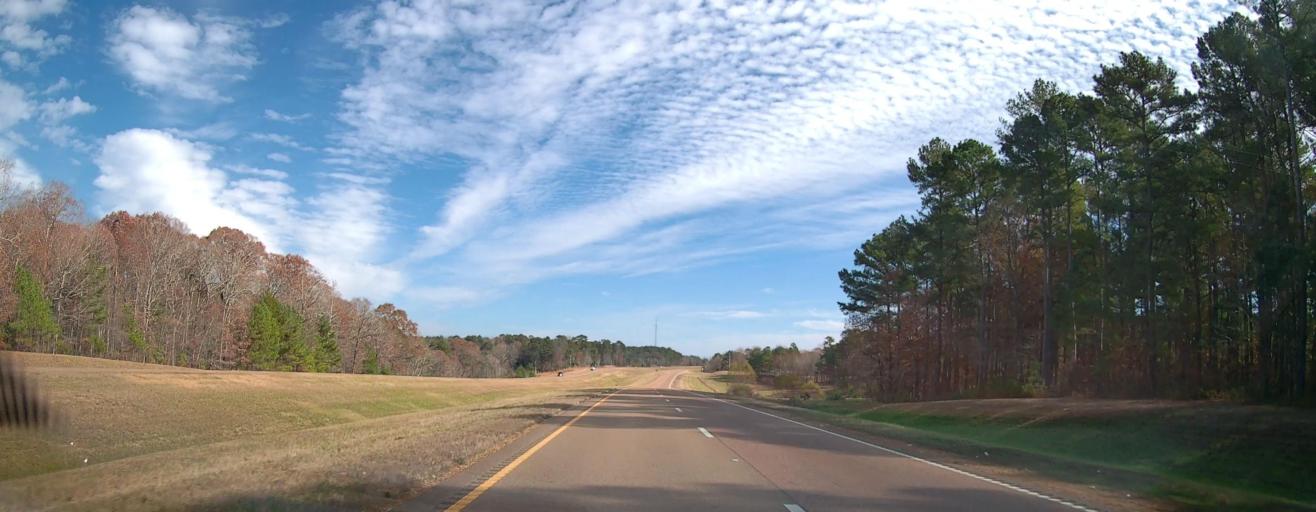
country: US
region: Mississippi
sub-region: Benton County
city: Ashland
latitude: 34.9542
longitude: -89.0314
